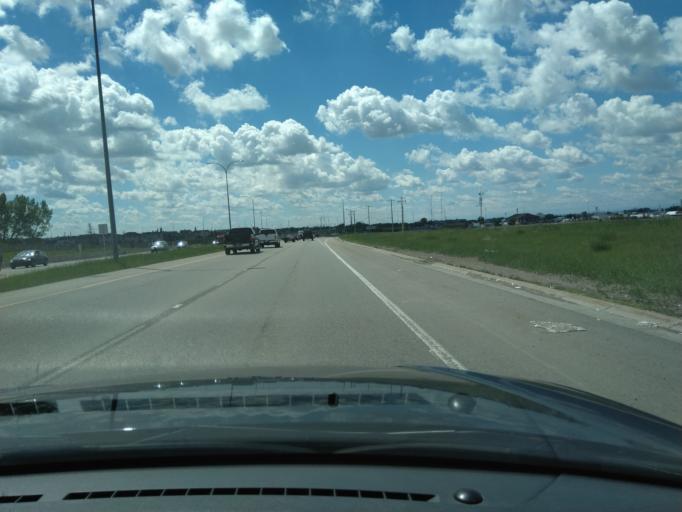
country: CA
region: Alberta
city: Calgary
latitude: 51.1286
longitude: -113.9704
